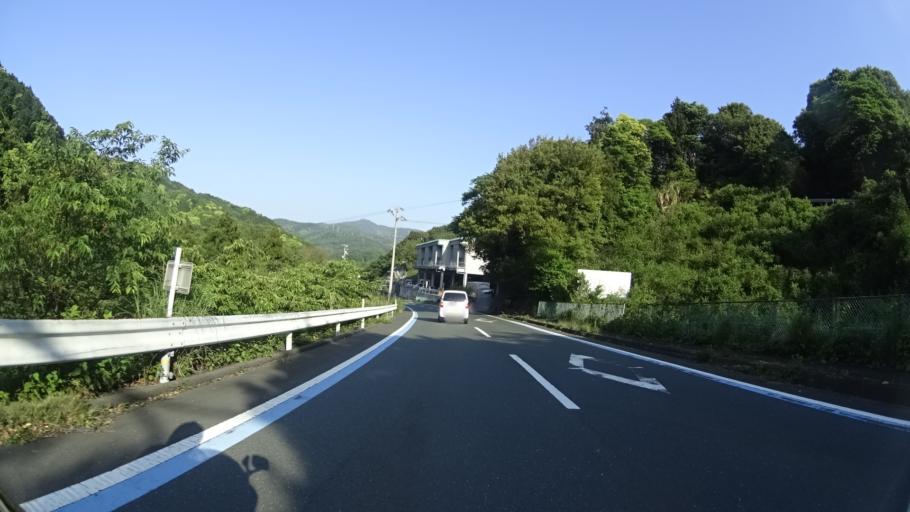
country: JP
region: Ehime
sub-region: Nishiuwa-gun
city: Ikata-cho
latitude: 33.3960
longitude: 132.1496
